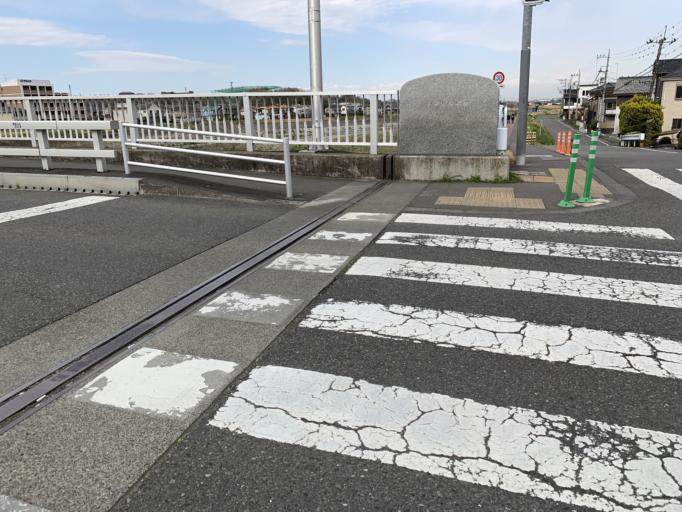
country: JP
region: Tokyo
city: Hino
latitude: 35.6598
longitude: 139.3934
